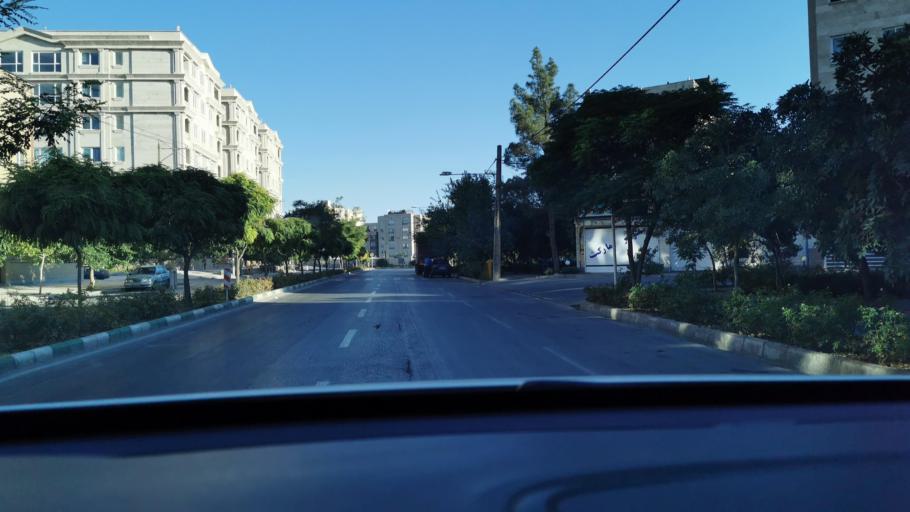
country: IR
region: Razavi Khorasan
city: Mashhad
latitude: 36.3594
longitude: 59.4845
